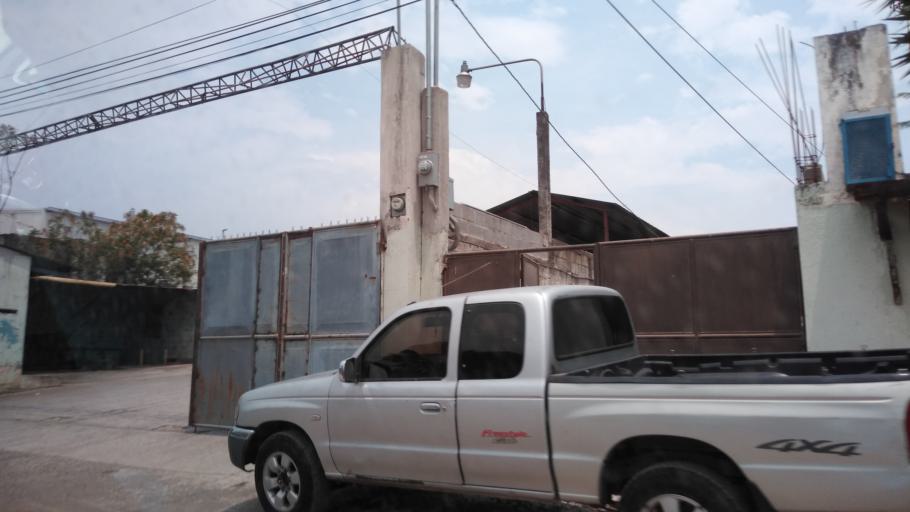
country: GT
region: Guatemala
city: Petapa
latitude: 14.5068
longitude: -90.5573
